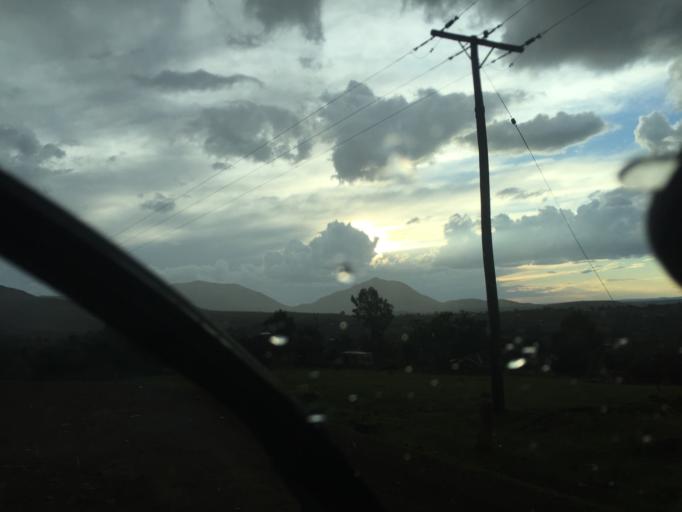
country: LS
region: Berea
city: Teyateyaneng
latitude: -29.1584
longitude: 28.0338
